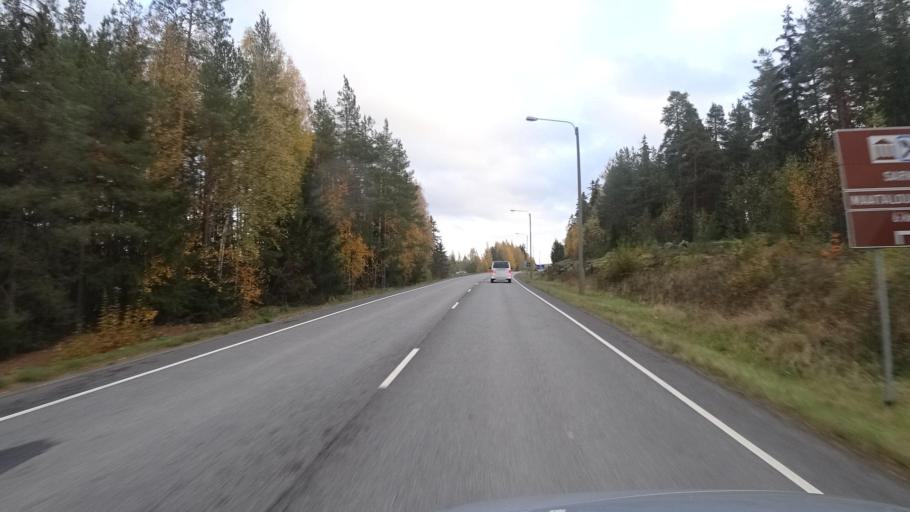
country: FI
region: Varsinais-Suomi
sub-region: Loimaa
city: Loimaa
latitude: 60.8740
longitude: 22.9975
